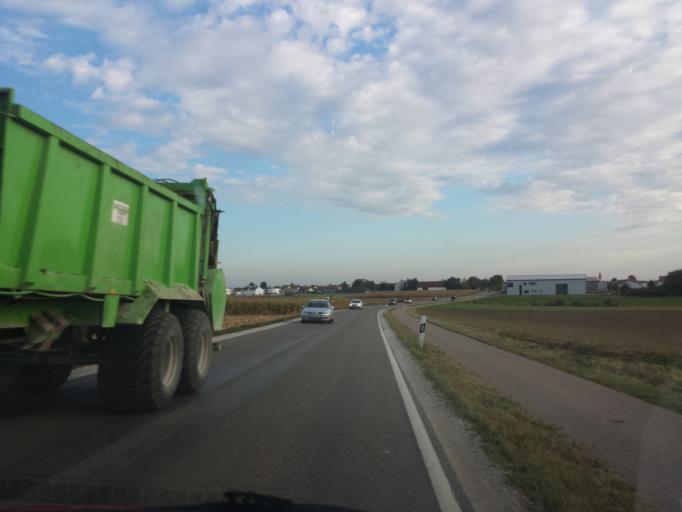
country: DE
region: Bavaria
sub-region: Upper Bavaria
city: Gaimersheim
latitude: 48.7653
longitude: 11.3440
